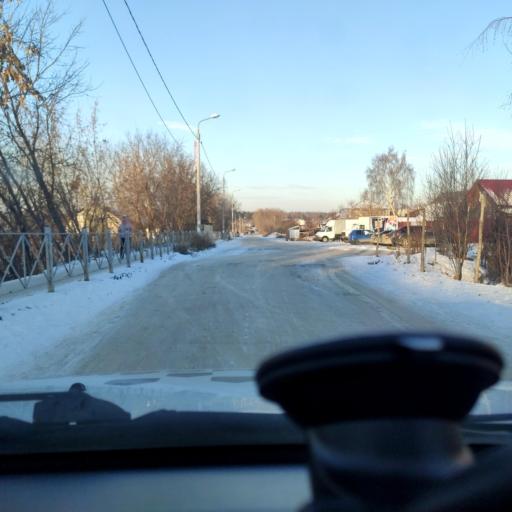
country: RU
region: Perm
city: Kondratovo
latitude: 57.9608
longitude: 56.1463
